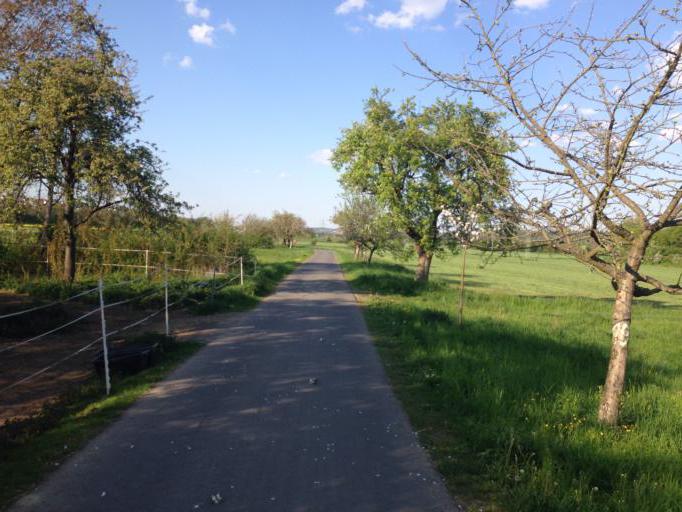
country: DE
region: Hesse
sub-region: Regierungsbezirk Giessen
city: Giessen
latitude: 50.6195
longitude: 8.6674
